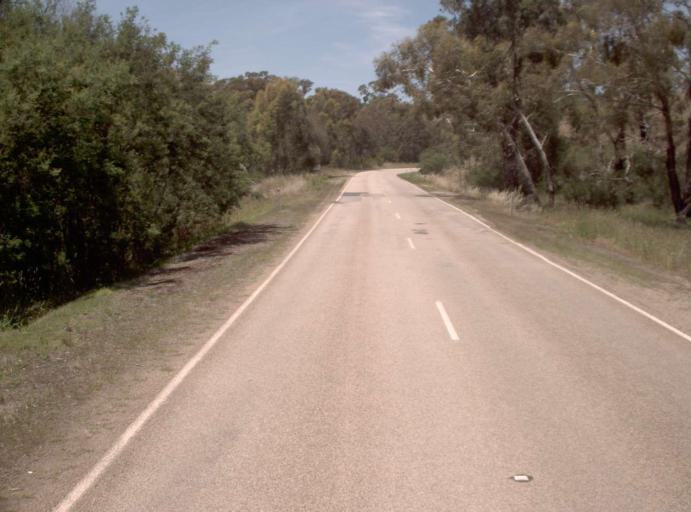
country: AU
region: Victoria
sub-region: East Gippsland
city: Bairnsdale
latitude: -37.3054
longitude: 147.7542
